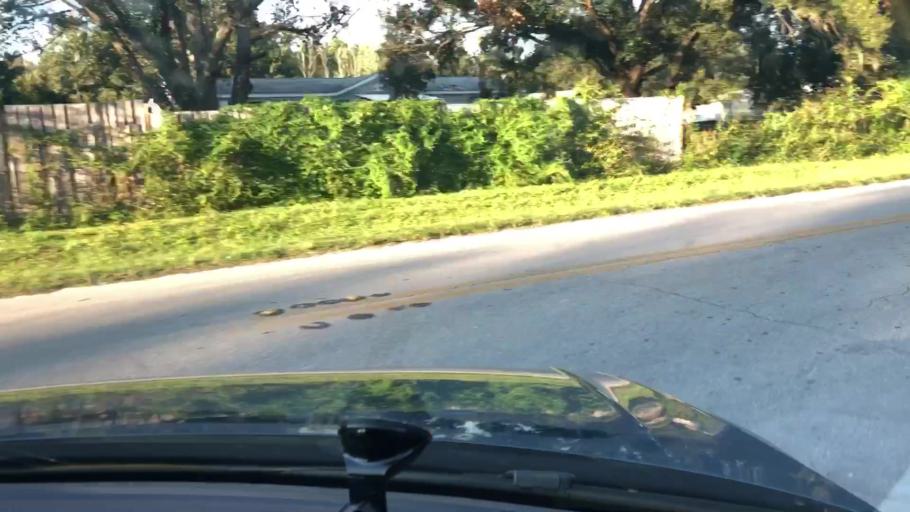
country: US
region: Florida
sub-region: Polk County
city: Kathleen
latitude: 28.1214
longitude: -82.0520
